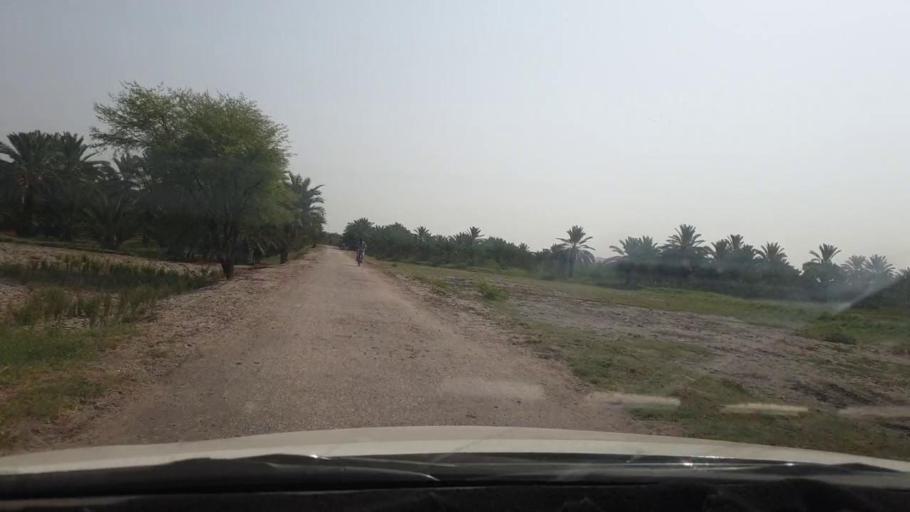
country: PK
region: Sindh
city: Rohri
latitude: 27.6114
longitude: 68.8959
